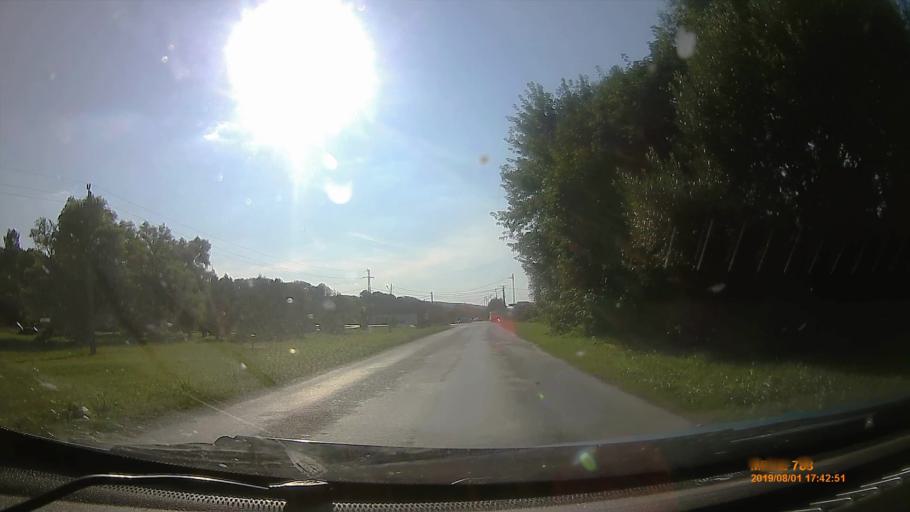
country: HU
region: Baranya
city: Sasd
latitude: 46.1911
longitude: 18.1556
